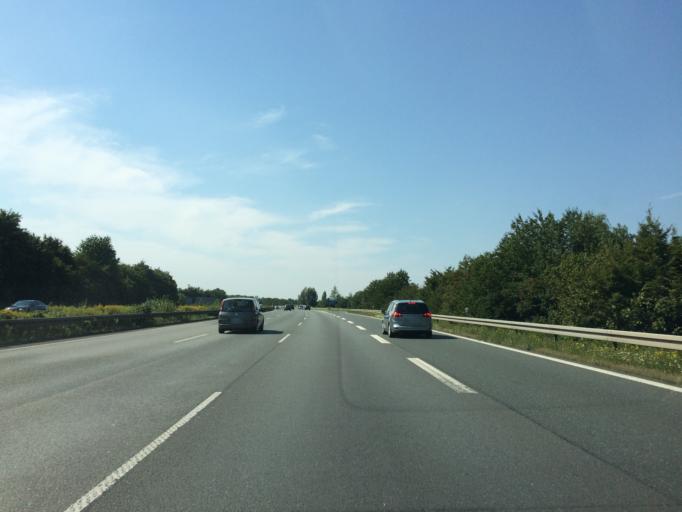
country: DE
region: North Rhine-Westphalia
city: Castrop-Rauxel
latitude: 51.6033
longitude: 7.3226
